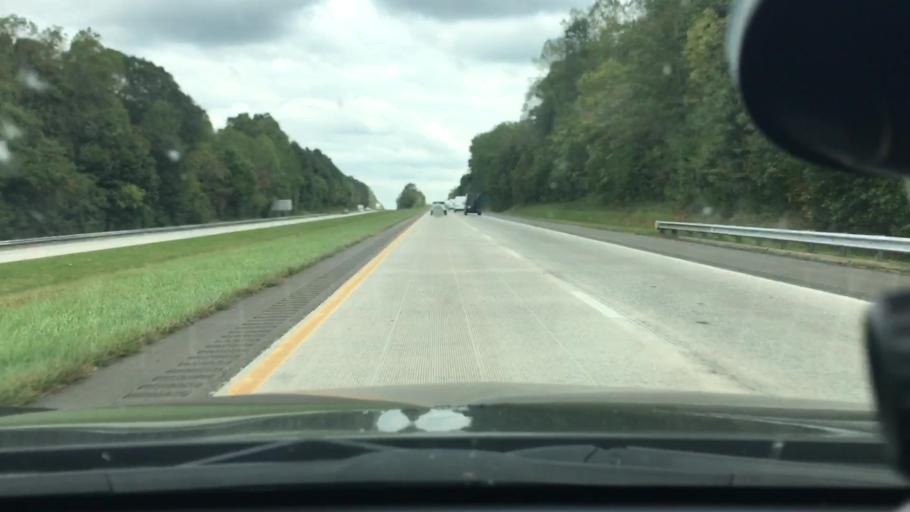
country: US
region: North Carolina
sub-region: Iredell County
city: Statesville
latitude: 35.8218
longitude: -80.8097
